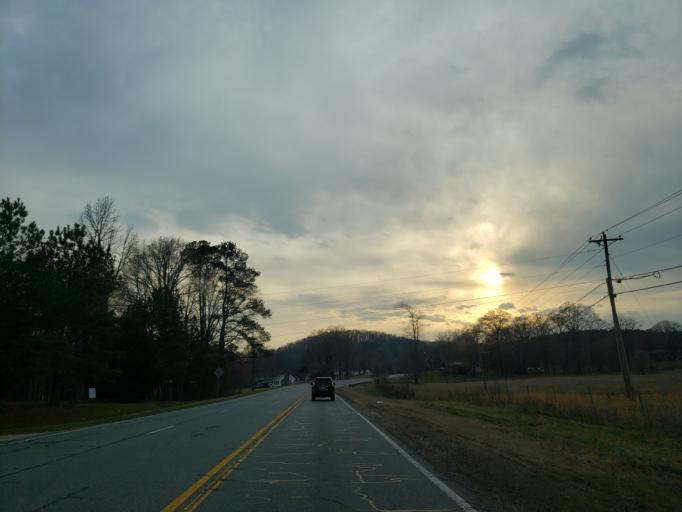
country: US
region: Georgia
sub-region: Whitfield County
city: Varnell
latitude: 34.8729
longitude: -85.0102
